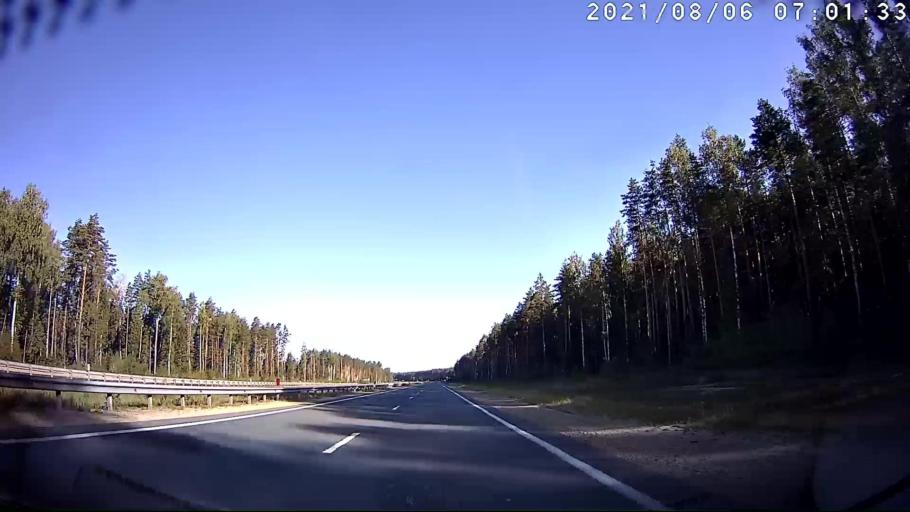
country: RU
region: Mariy-El
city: Surok
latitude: 56.5243
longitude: 48.0085
